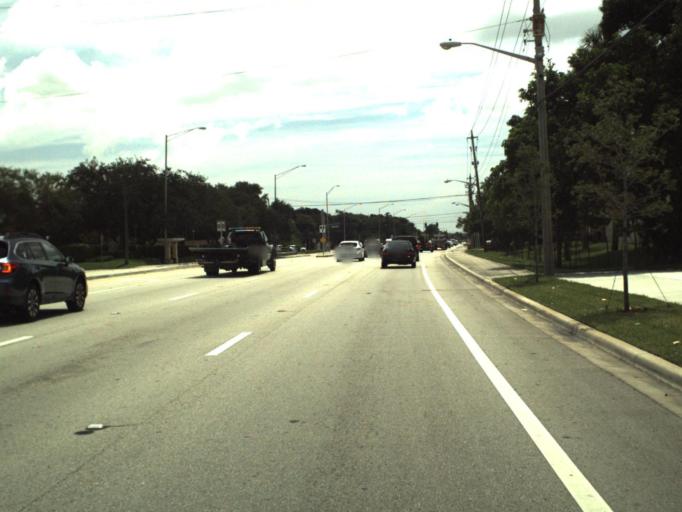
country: US
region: Florida
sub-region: Broward County
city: Margate
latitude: 26.2350
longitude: -80.1971
